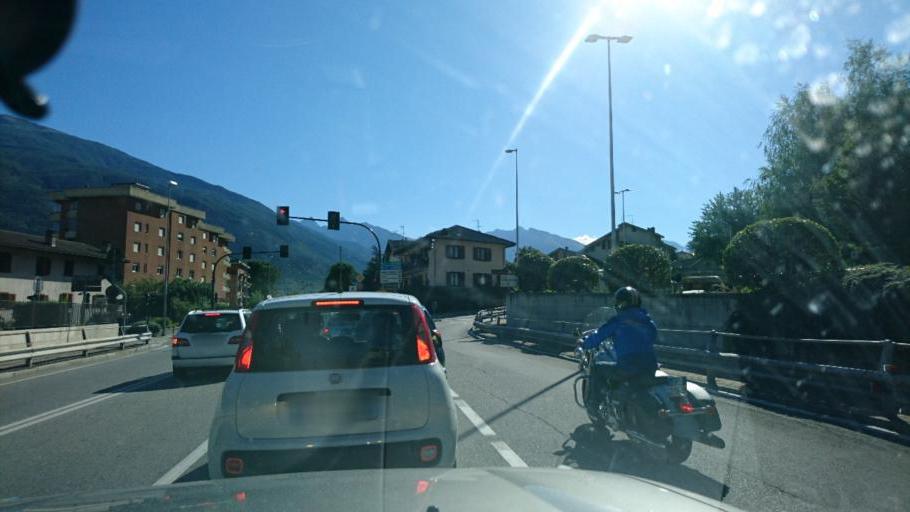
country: IT
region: Aosta Valley
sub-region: Valle d'Aosta
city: Gressan
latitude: 45.7334
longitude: 7.2918
